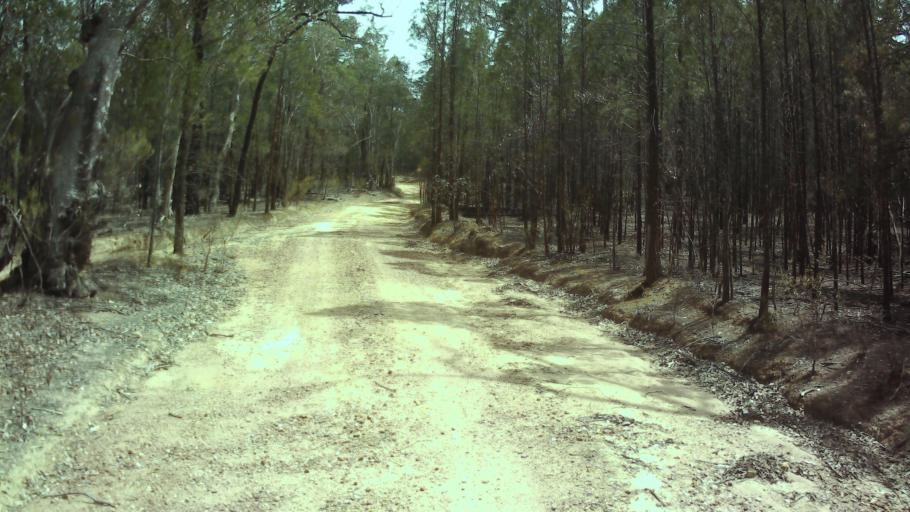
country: AU
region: New South Wales
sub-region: Weddin
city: Grenfell
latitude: -33.8866
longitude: 148.3830
